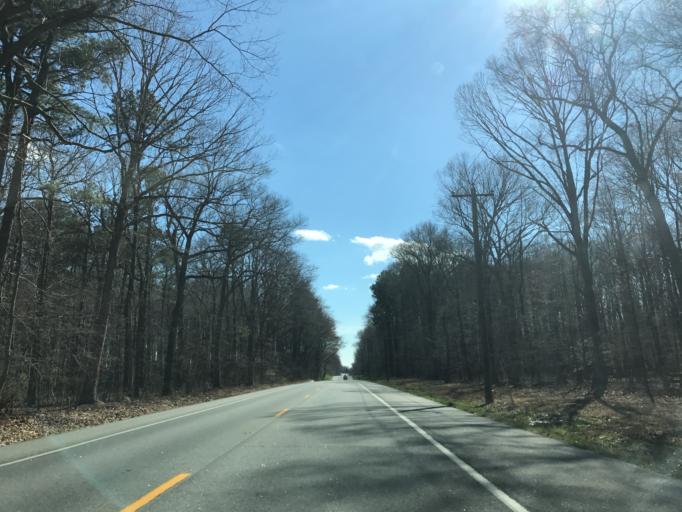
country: US
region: Maryland
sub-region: Kent County
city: Rock Hall
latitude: 39.1909
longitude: -76.1922
